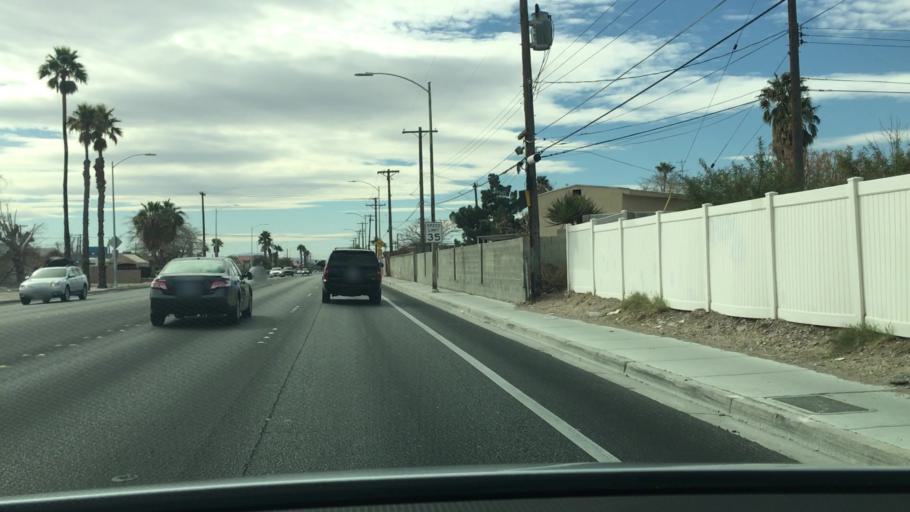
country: US
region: Nevada
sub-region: Clark County
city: Spring Valley
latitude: 36.1657
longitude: -115.2239
